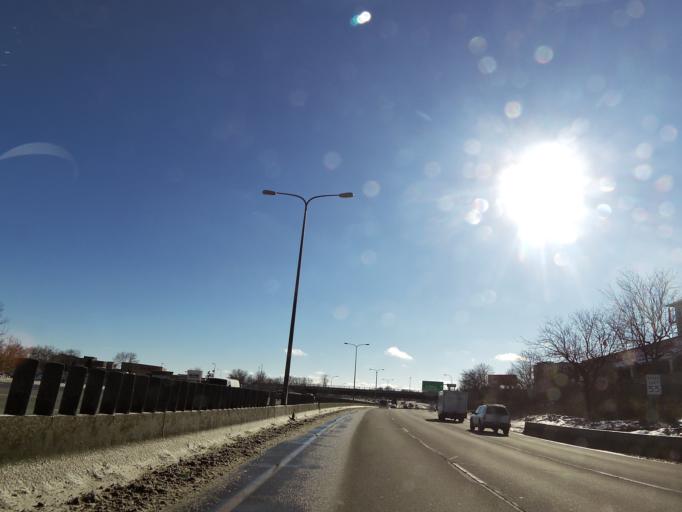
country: US
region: Minnesota
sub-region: Hennepin County
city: Saint Louis Park
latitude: 44.9403
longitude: -93.3483
